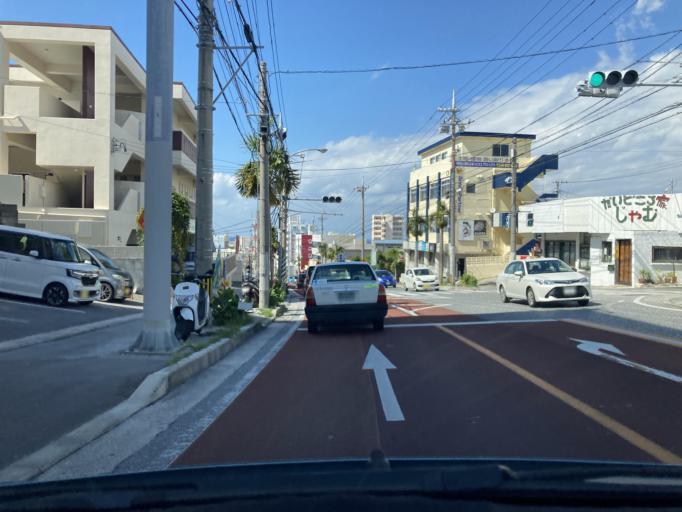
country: JP
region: Okinawa
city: Ginowan
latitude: 26.2648
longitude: 127.7390
